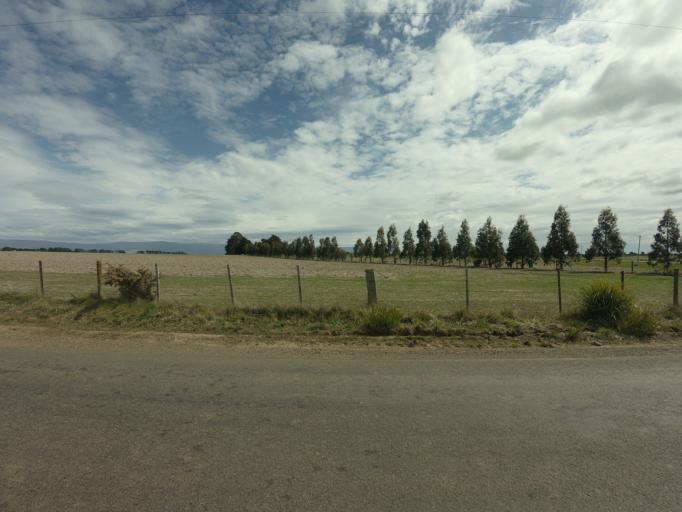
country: AU
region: Tasmania
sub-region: Northern Midlands
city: Longford
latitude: -41.7035
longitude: 147.1964
